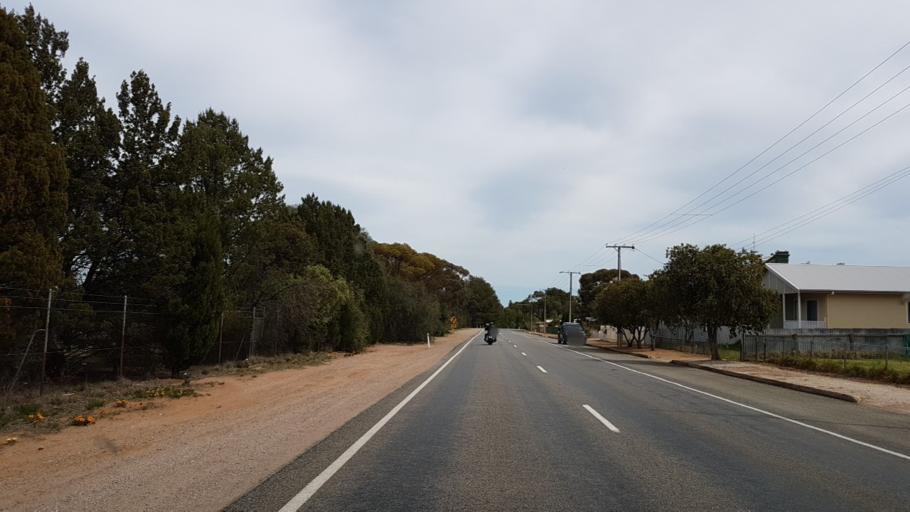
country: AU
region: South Australia
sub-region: Port Pirie City and Dists
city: Crystal Brook
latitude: -33.2624
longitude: 138.3536
